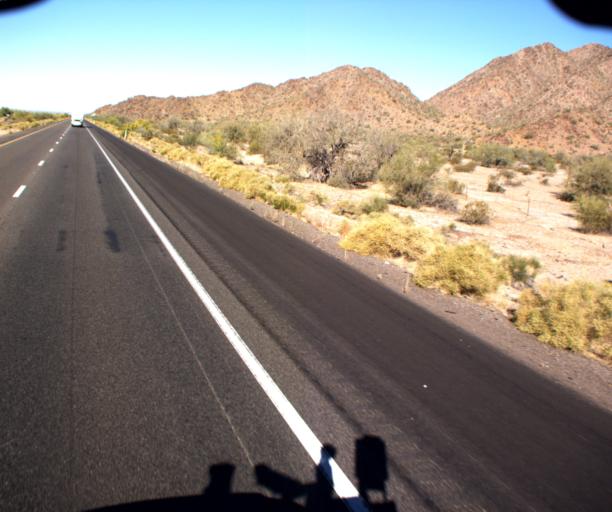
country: US
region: Arizona
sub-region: Maricopa County
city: Gila Bend
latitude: 32.9069
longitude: -112.5560
